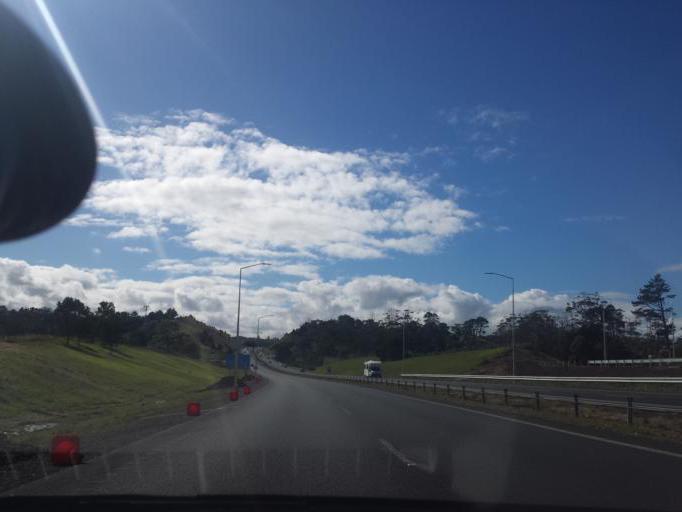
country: NZ
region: Auckland
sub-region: Auckland
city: Rothesay Bay
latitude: -36.6027
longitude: 174.6622
